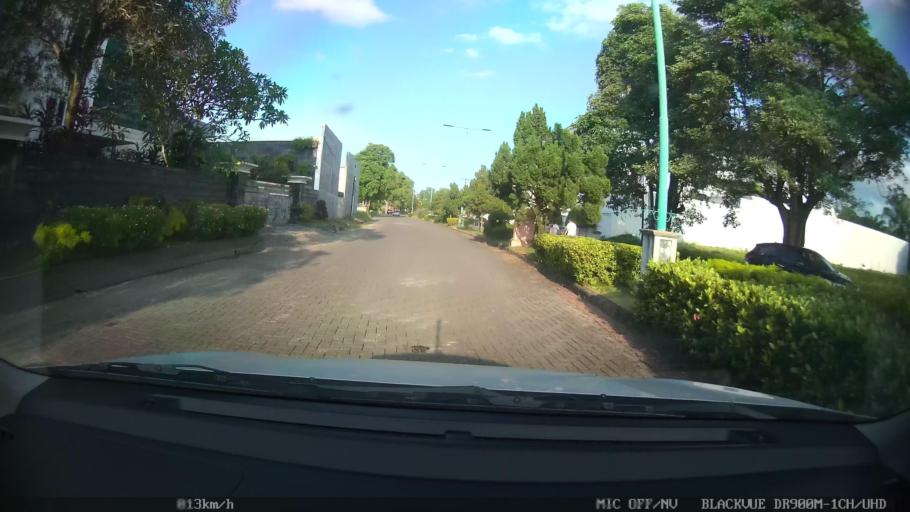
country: ID
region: North Sumatra
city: Medan
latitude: 3.6242
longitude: 98.6534
